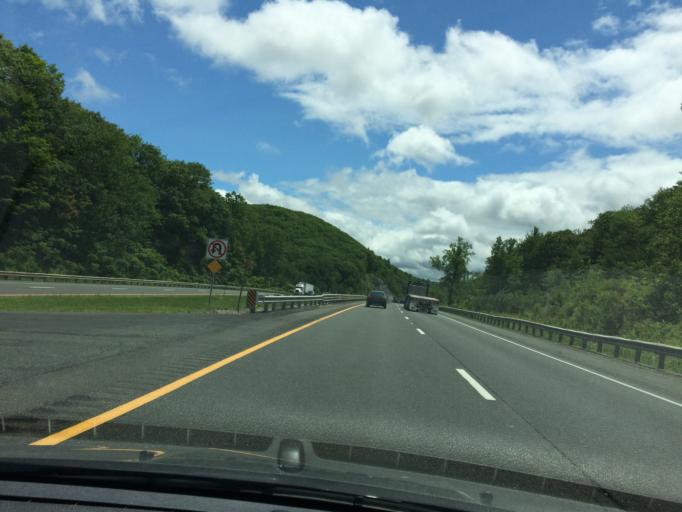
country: US
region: Massachusetts
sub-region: Berkshire County
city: Becket
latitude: 42.2793
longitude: -73.1455
